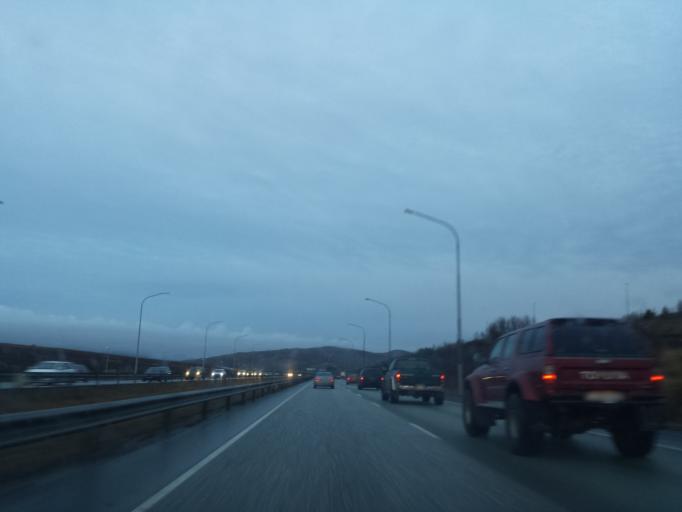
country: IS
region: Capital Region
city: Mosfellsbaer
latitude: 64.1272
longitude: -21.7764
